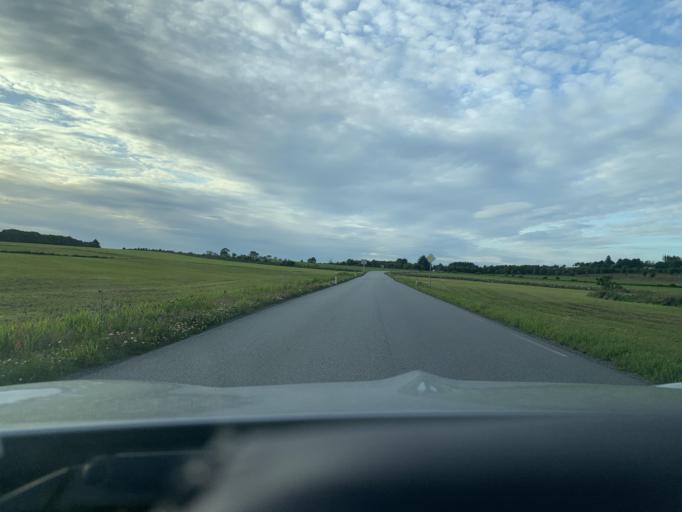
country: NO
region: Rogaland
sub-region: Time
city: Bryne
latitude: 58.6931
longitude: 5.7106
